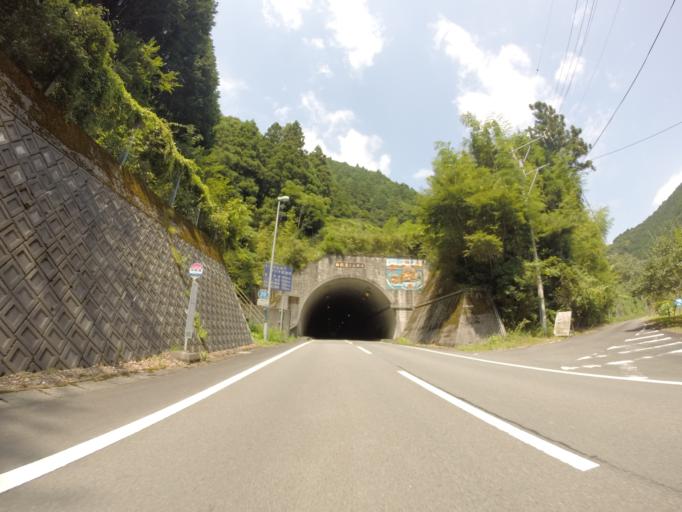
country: JP
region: Shizuoka
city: Shizuoka-shi
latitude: 35.2247
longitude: 138.3488
